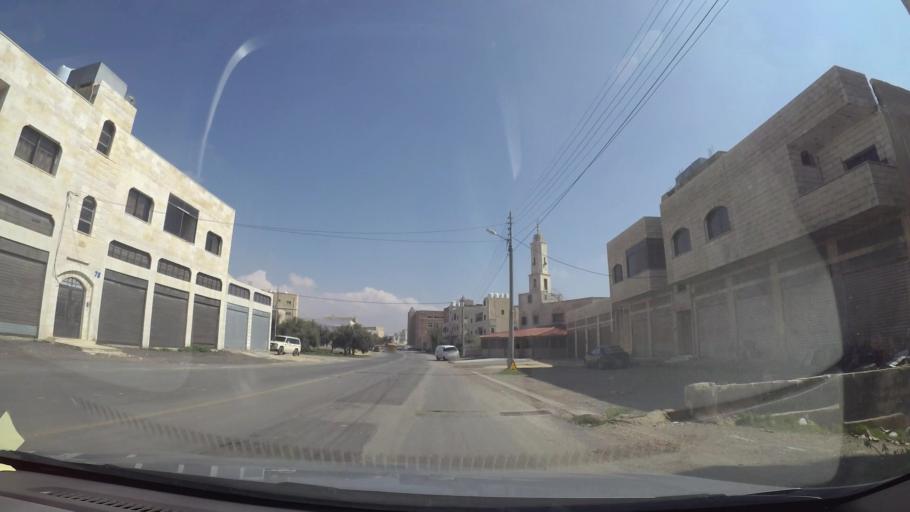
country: JO
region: Amman
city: Al Bunayyat ash Shamaliyah
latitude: 31.8982
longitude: 35.9020
